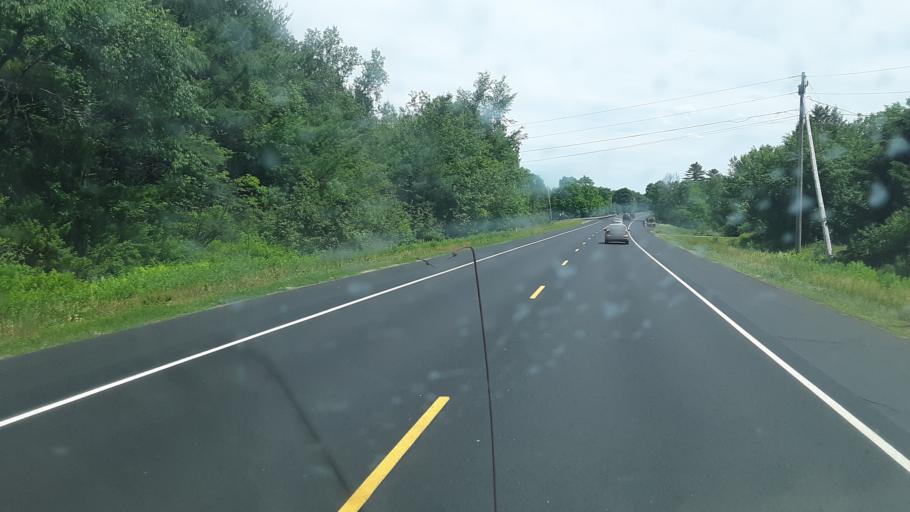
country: US
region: Maine
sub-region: Somerset County
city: Norridgewock
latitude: 44.6825
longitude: -69.7269
